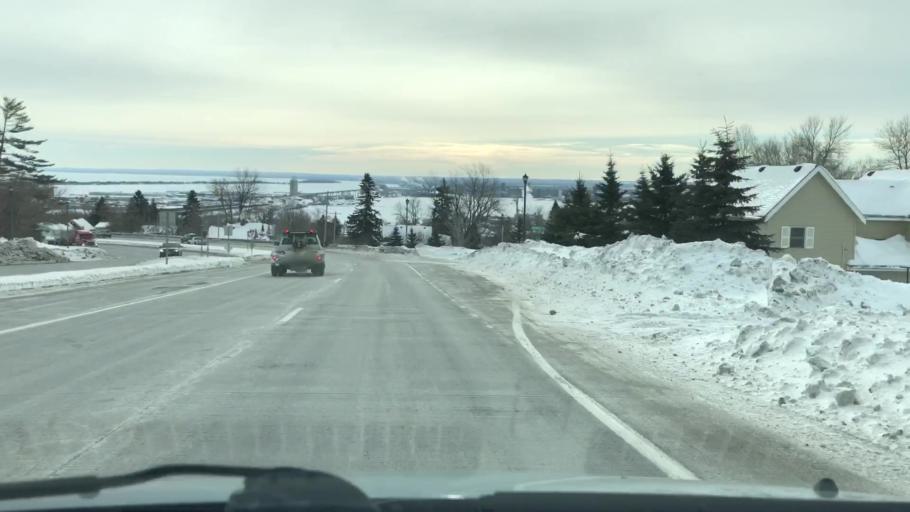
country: US
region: Minnesota
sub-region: Saint Louis County
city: Duluth
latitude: 46.7720
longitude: -92.1383
